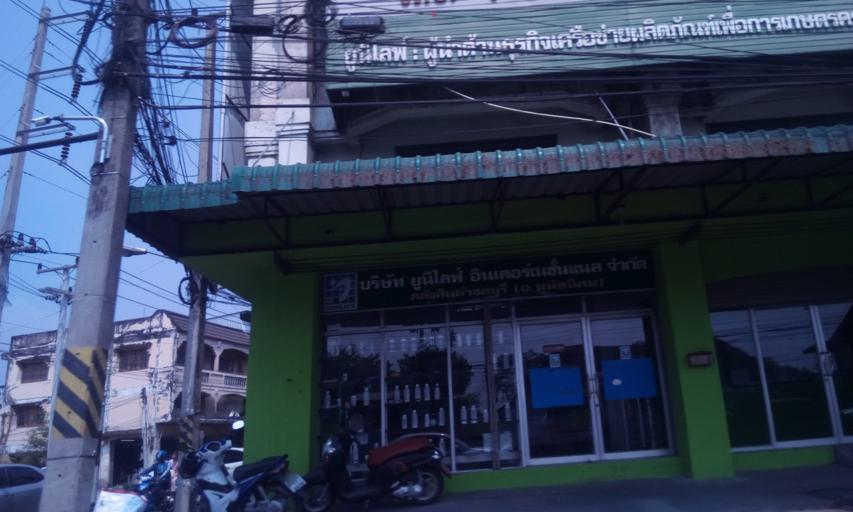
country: TH
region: Chon Buri
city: Phanat Nikhom
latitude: 13.4399
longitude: 101.1789
